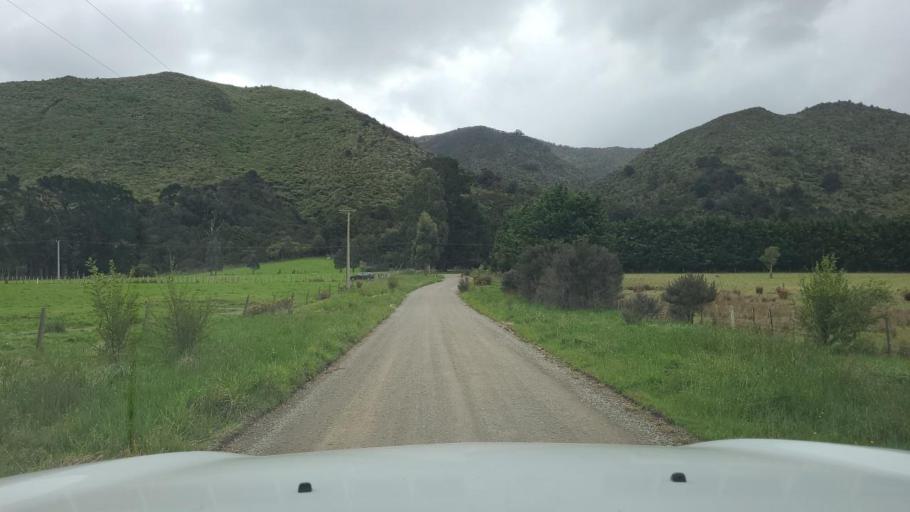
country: NZ
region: Wellington
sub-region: Upper Hutt City
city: Upper Hutt
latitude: -41.0814
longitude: 175.3524
